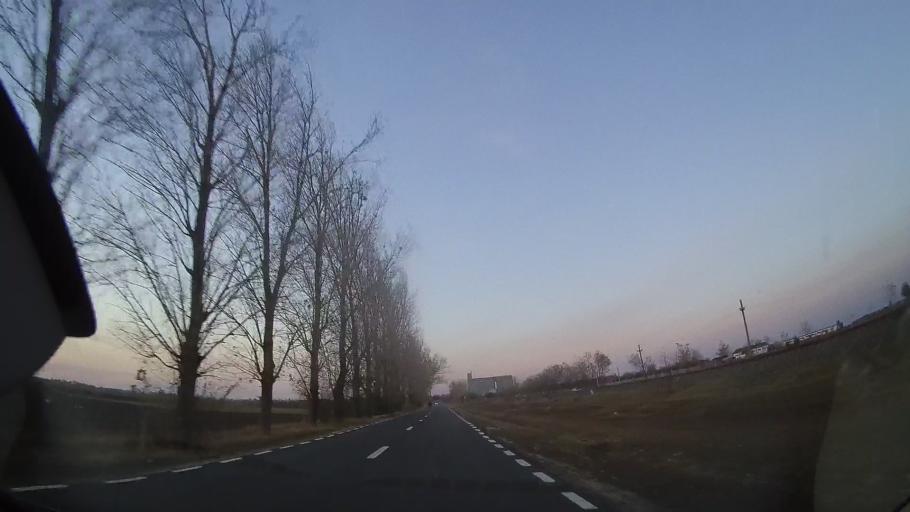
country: RO
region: Constanta
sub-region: Comuna Cobadin
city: Cobadin
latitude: 44.0462
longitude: 28.2524
